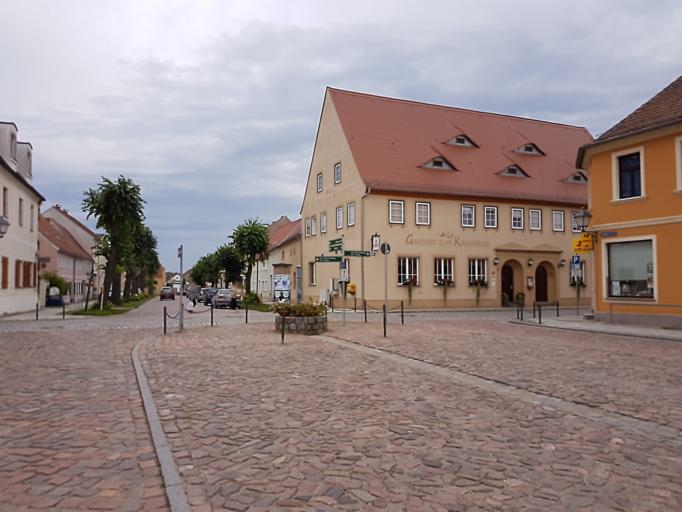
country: DE
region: Brandenburg
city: Muhlberg
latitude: 51.4352
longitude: 13.2185
